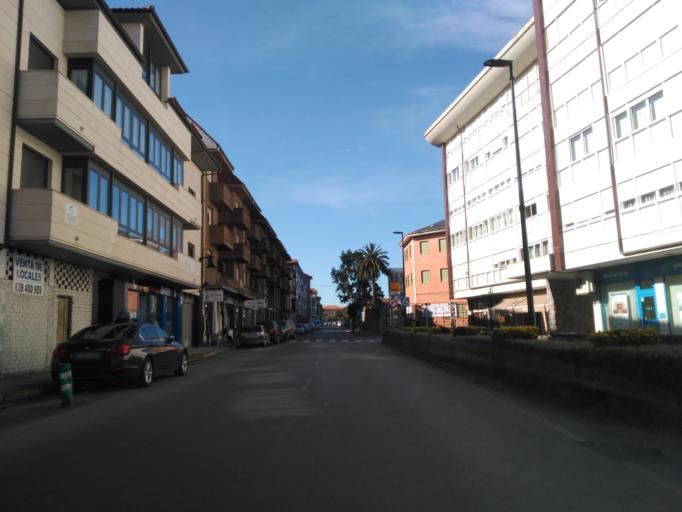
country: ES
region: Asturias
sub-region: Province of Asturias
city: Llanes
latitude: 43.4216
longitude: -4.7586
